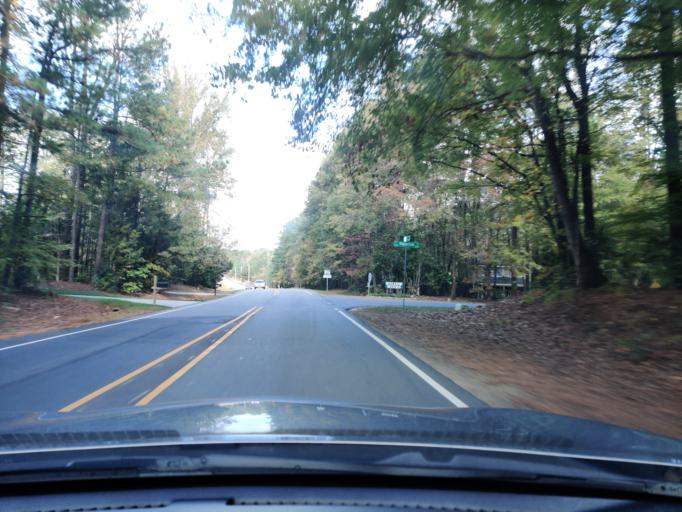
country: US
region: North Carolina
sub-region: Wake County
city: West Raleigh
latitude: 35.9130
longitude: -78.7055
